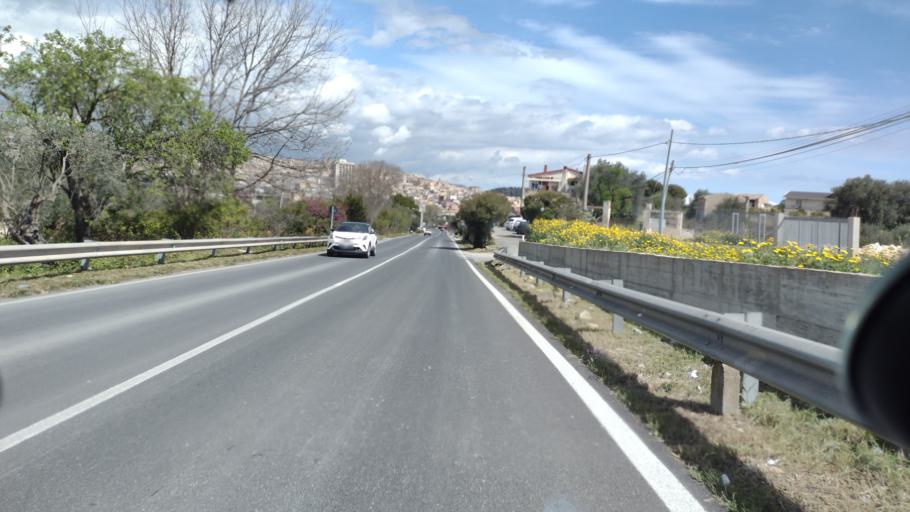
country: IT
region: Sicily
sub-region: Provincia di Siracusa
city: Noto
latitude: 36.8798
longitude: 15.0600
